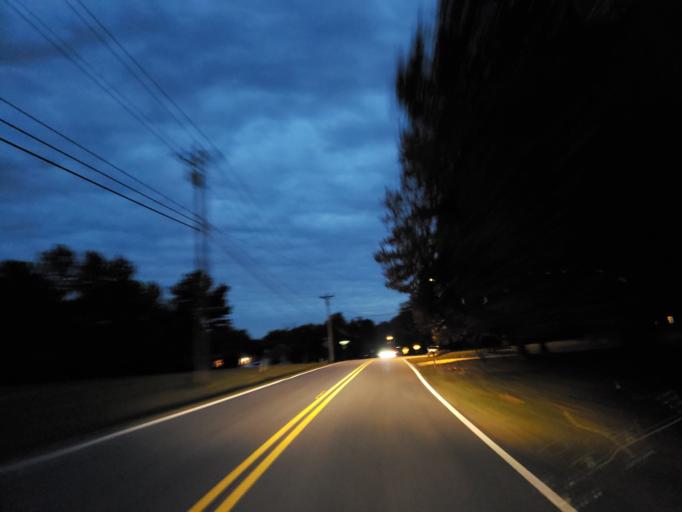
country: US
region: Georgia
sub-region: Cobb County
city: Powder Springs
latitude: 33.8988
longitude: -84.7067
